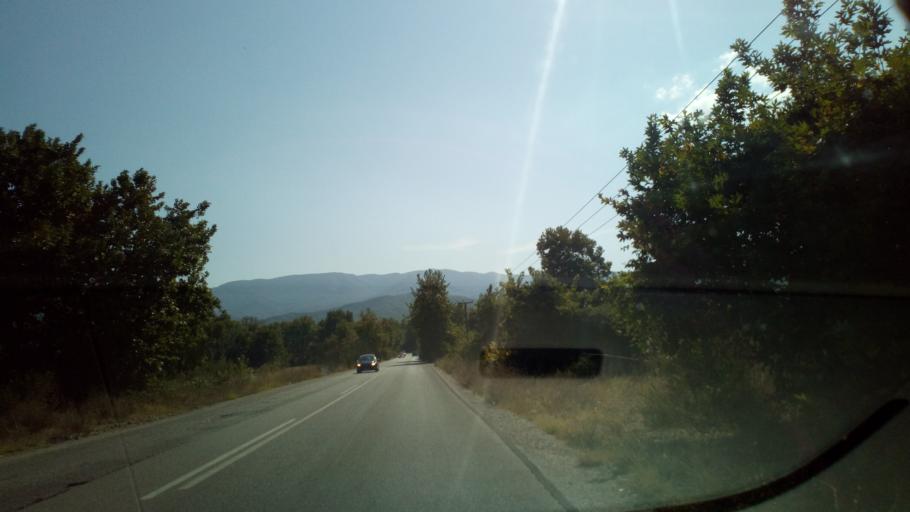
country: GR
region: Central Macedonia
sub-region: Nomos Thessalonikis
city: Stavros
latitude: 40.6022
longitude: 23.7717
